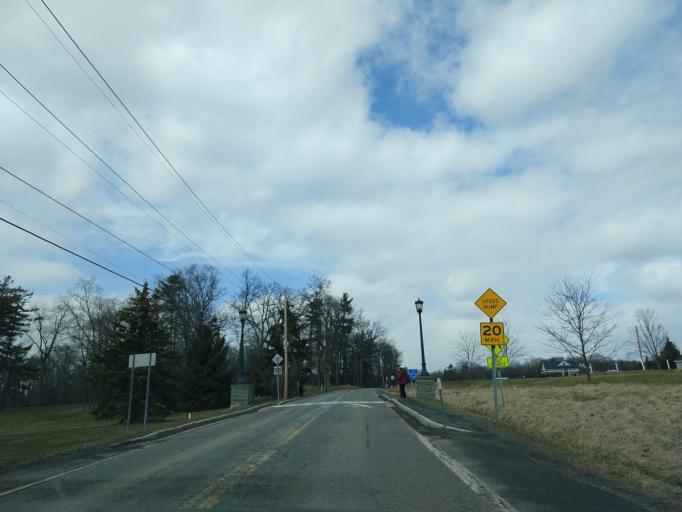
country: US
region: New York
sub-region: Tompkins County
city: Northeast Ithaca
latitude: 42.4560
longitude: -76.4685
